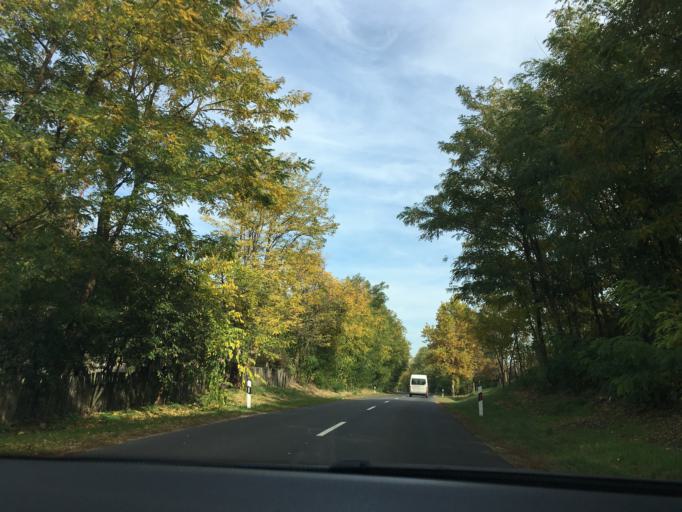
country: HU
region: Szabolcs-Szatmar-Bereg
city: Ujfeherto
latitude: 47.8306
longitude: 21.7407
